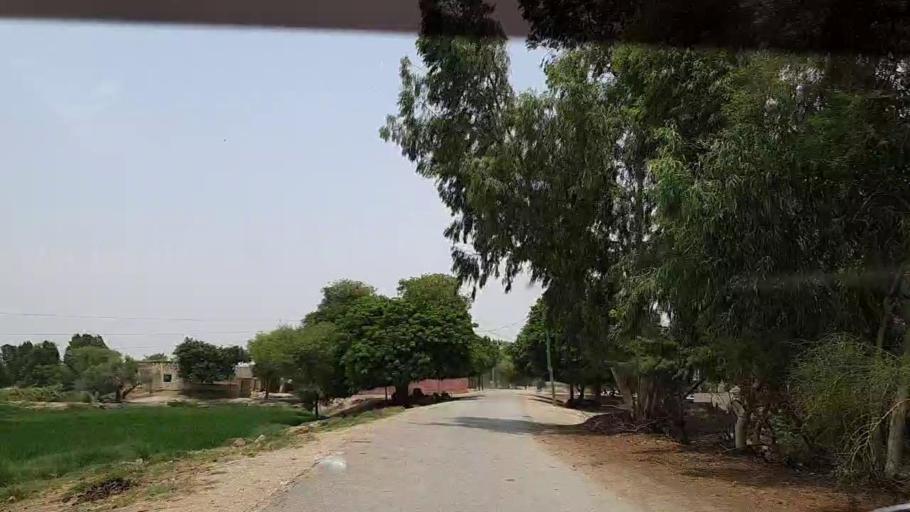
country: PK
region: Sindh
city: Khairpur Nathan Shah
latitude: 27.0170
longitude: 67.6695
